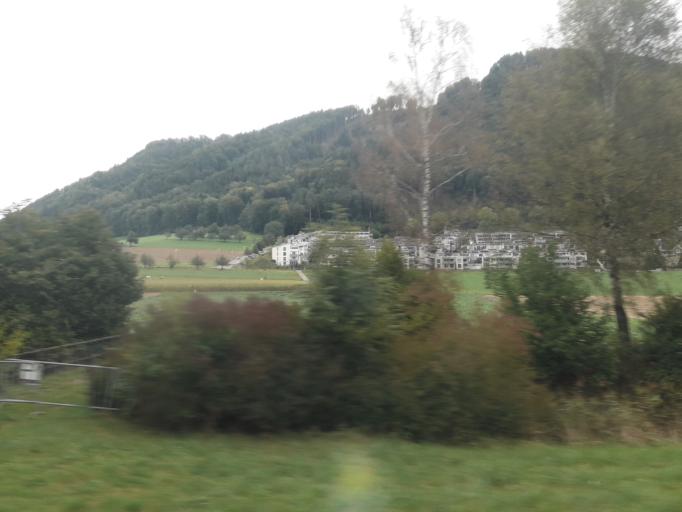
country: CH
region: Bern
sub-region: Bern-Mittelland District
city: Belp
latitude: 46.8817
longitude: 7.5002
